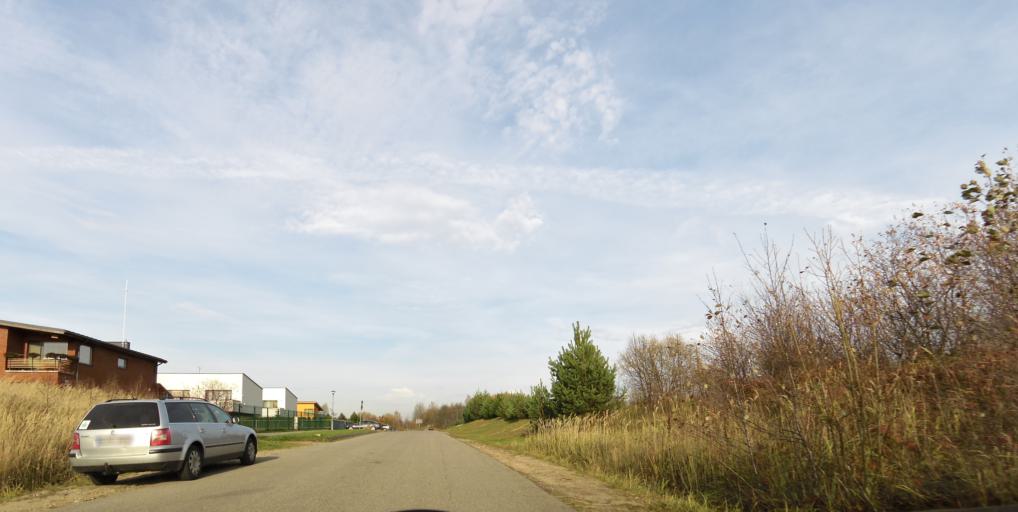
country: LT
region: Vilnius County
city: Justiniskes
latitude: 54.7128
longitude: 25.2060
